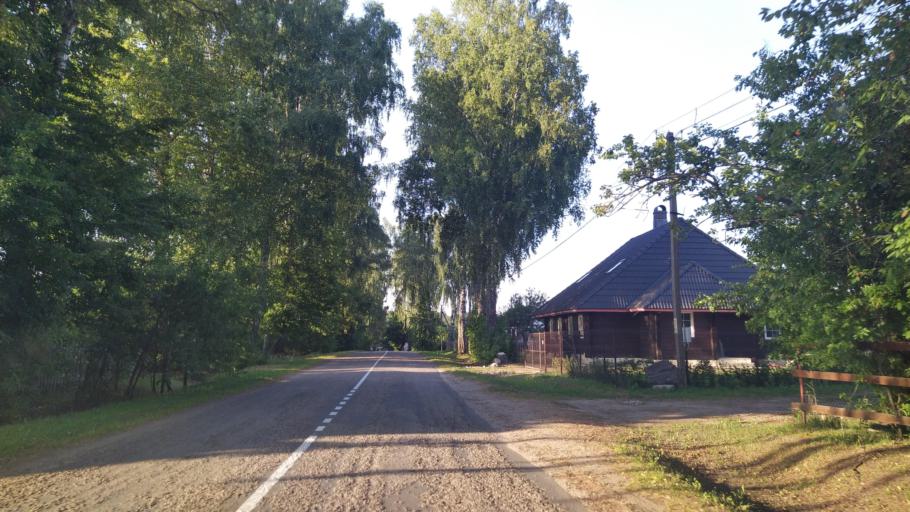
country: RU
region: Pskov
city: Pushkinskiye Gory
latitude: 57.0437
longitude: 28.9165
